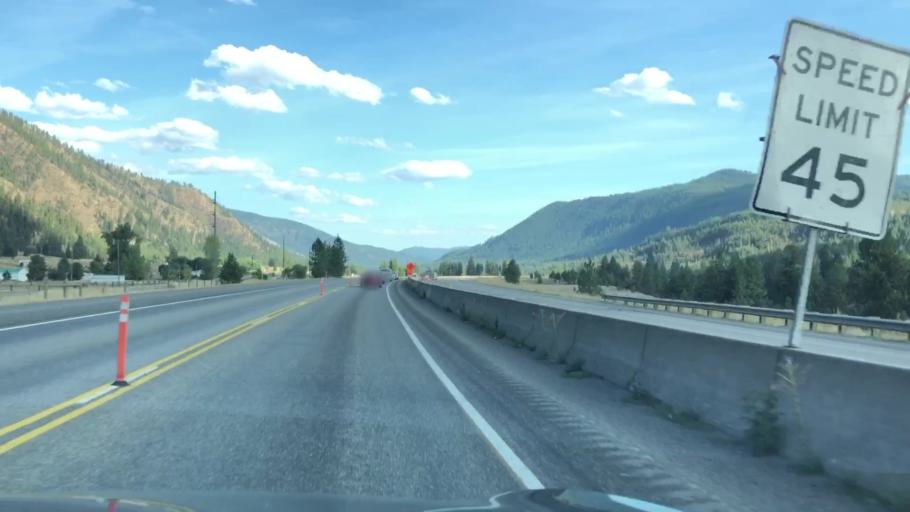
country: US
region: Montana
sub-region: Mineral County
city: Superior
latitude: 47.2148
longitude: -114.9447
